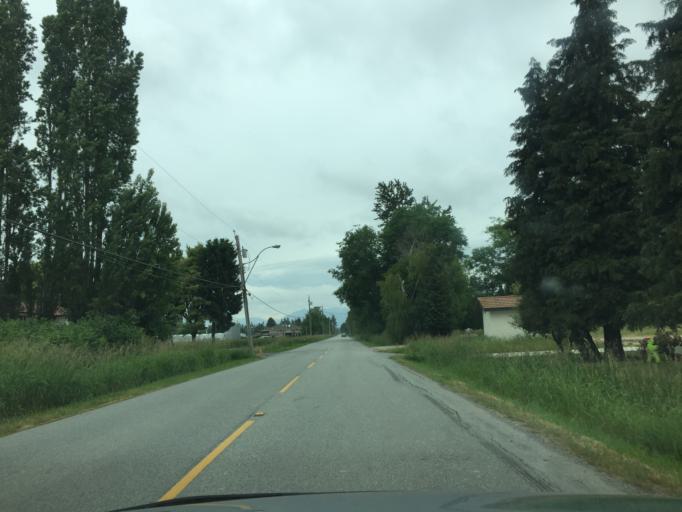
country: CA
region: British Columbia
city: Ladner
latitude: 49.1453
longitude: -123.0807
